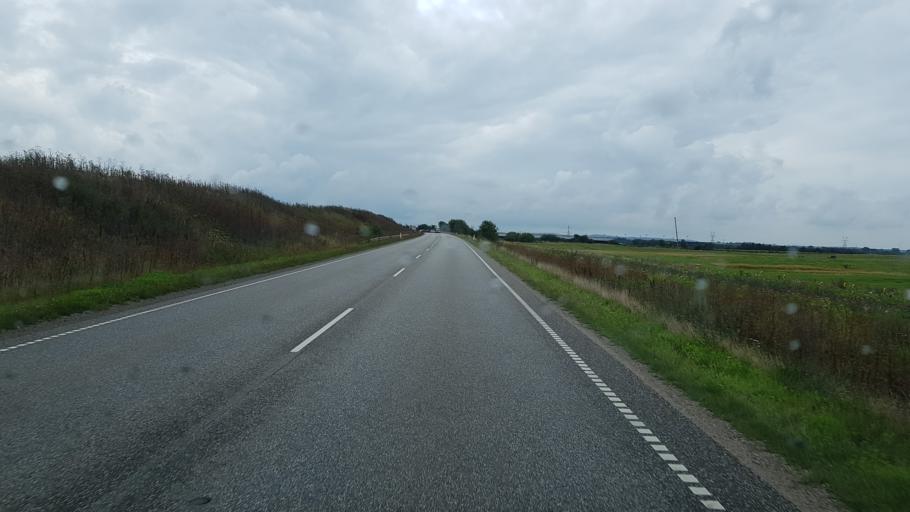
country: DK
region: Central Jutland
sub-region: Horsens Kommune
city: Horsens
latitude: 55.8935
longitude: 9.7587
